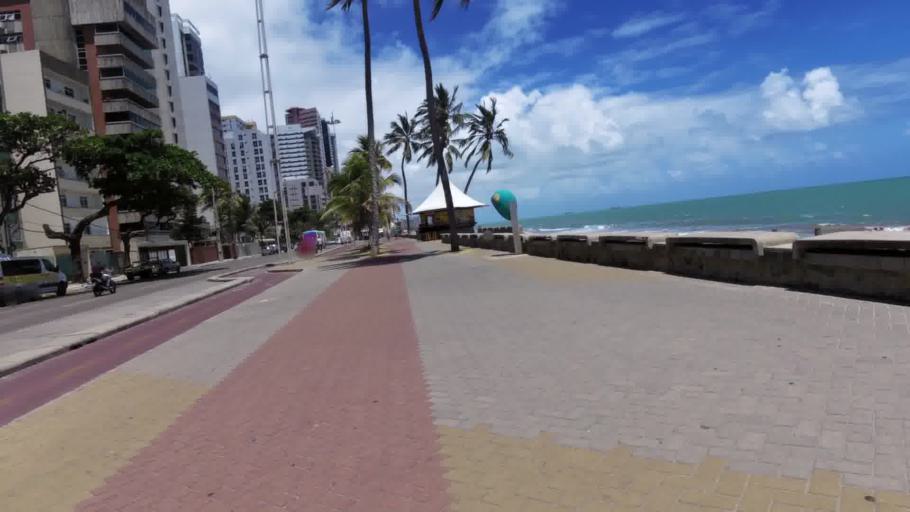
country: BR
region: Pernambuco
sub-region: Recife
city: Recife
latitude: -8.1407
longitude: -34.9030
